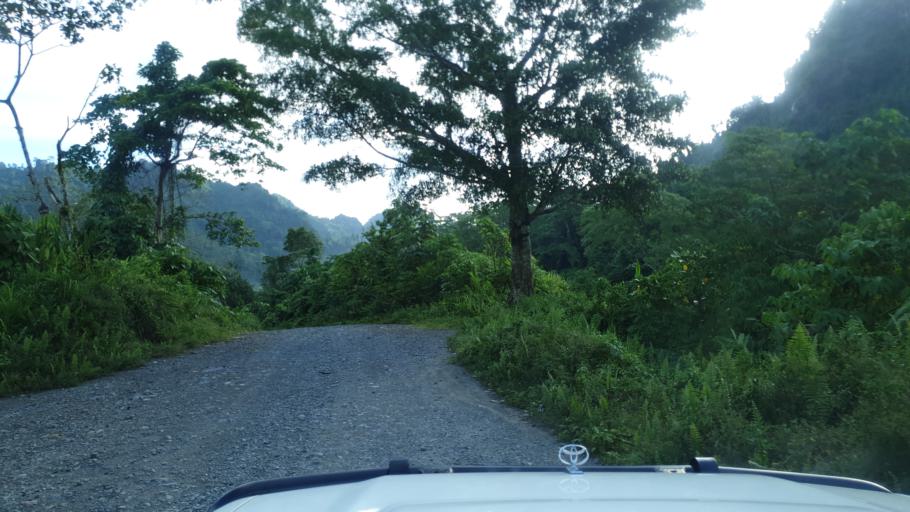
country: PG
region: Bougainville
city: Panguna
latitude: -6.3776
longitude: 155.4358
